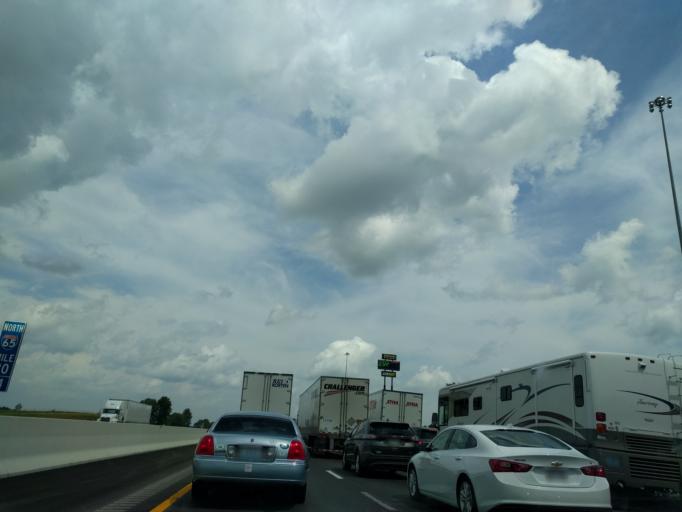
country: US
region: Kentucky
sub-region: Larue County
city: Hodgenville
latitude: 37.5226
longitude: -85.8846
